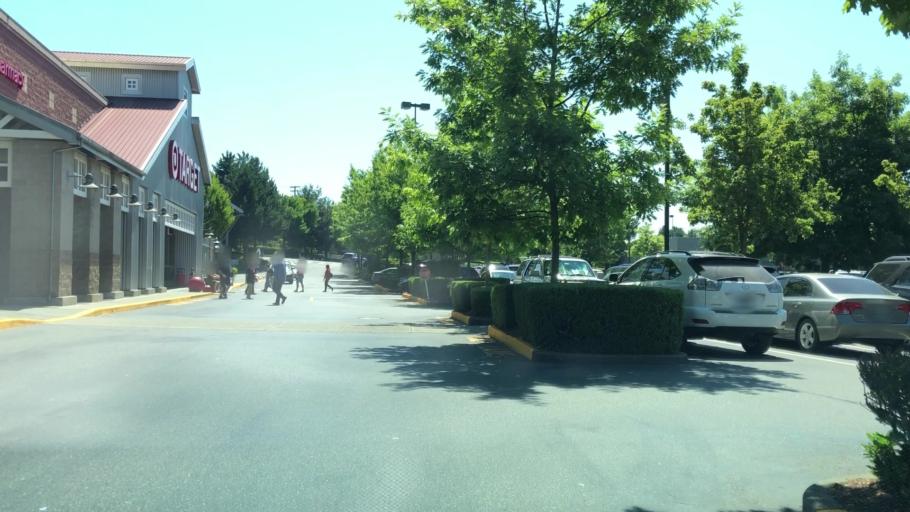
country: US
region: Washington
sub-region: King County
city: Woodinville
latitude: 47.7587
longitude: -122.1547
